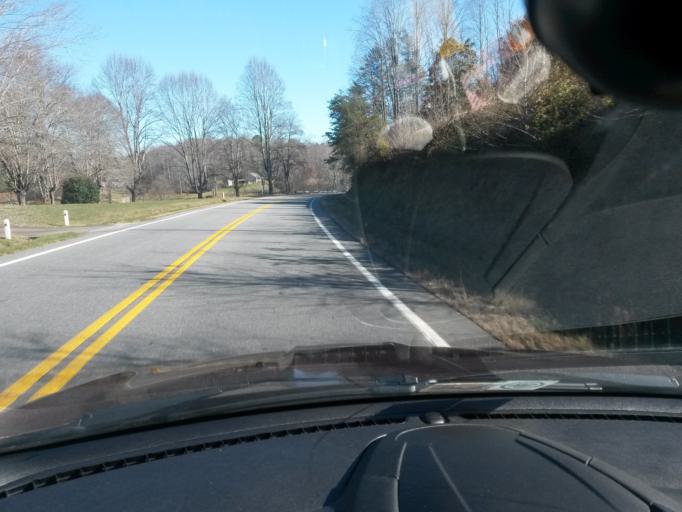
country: US
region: Virginia
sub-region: Henry County
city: Pannill Fork
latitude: 36.7812
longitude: -80.1319
